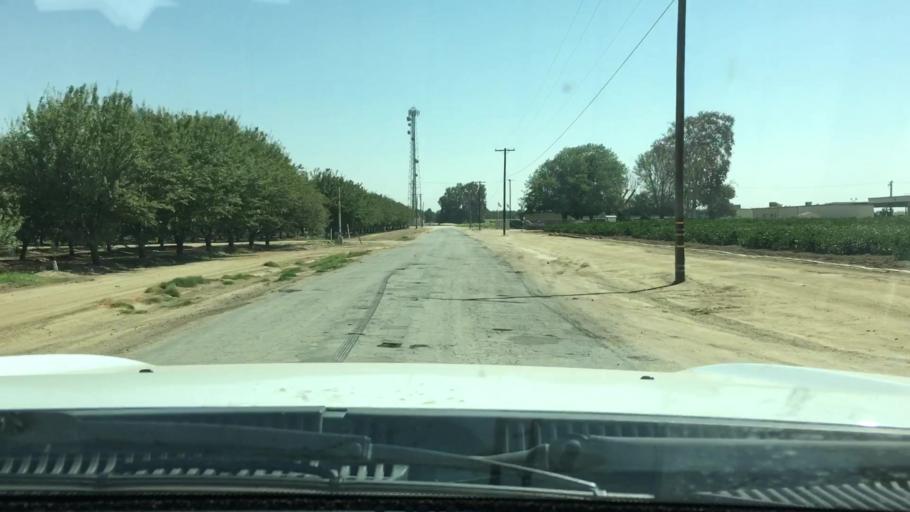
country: US
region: California
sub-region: Kern County
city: Shafter
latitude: 35.5364
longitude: -119.2719
